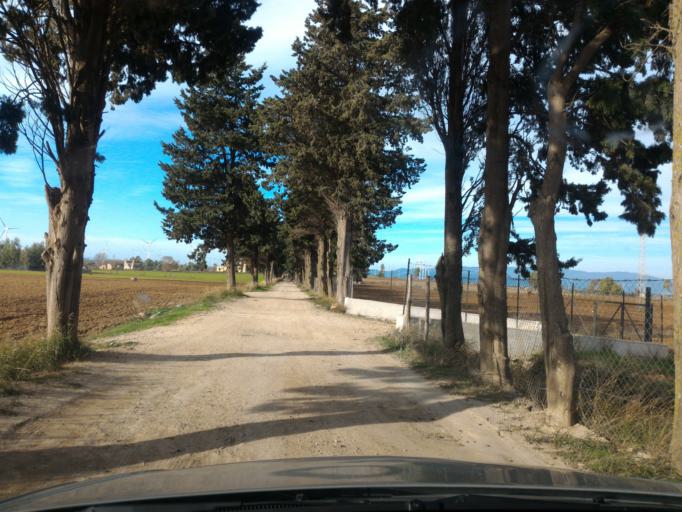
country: IT
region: Calabria
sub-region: Provincia di Crotone
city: Isola di Capo Rizzuto
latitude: 38.9872
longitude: 17.0686
